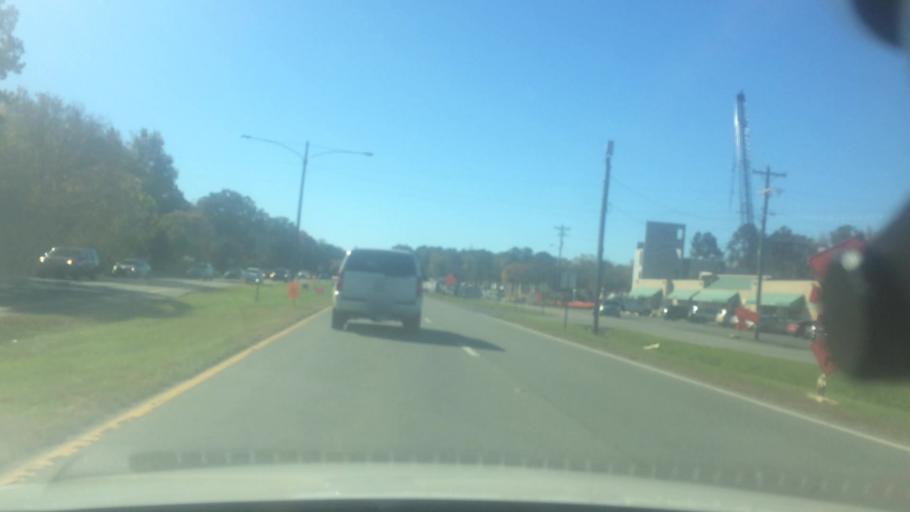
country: US
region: North Carolina
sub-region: Orange County
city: Chapel Hill
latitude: 35.9354
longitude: -79.0237
